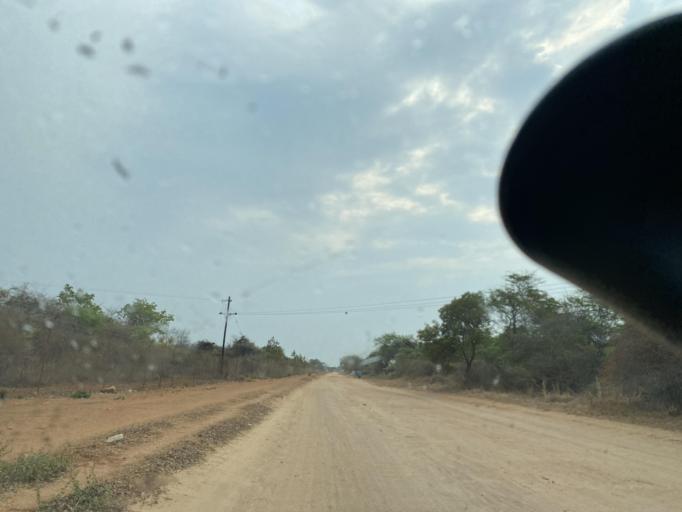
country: ZM
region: Lusaka
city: Lusaka
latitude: -15.2866
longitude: 28.2936
